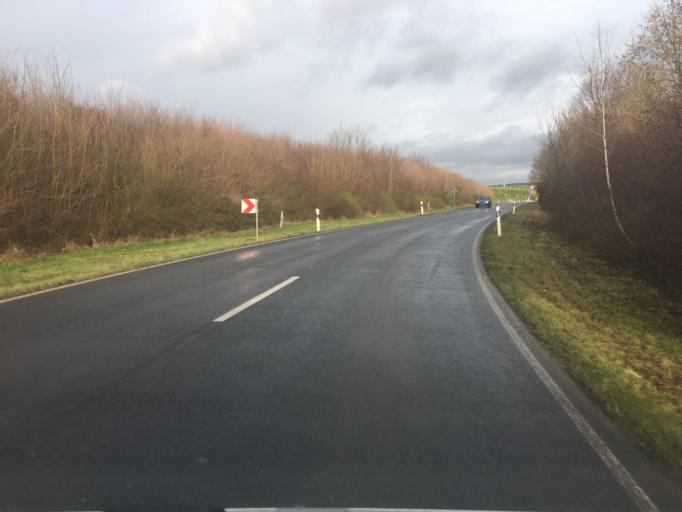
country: DE
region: North Rhine-Westphalia
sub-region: Regierungsbezirk Koln
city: Inden
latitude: 50.8469
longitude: 6.4137
